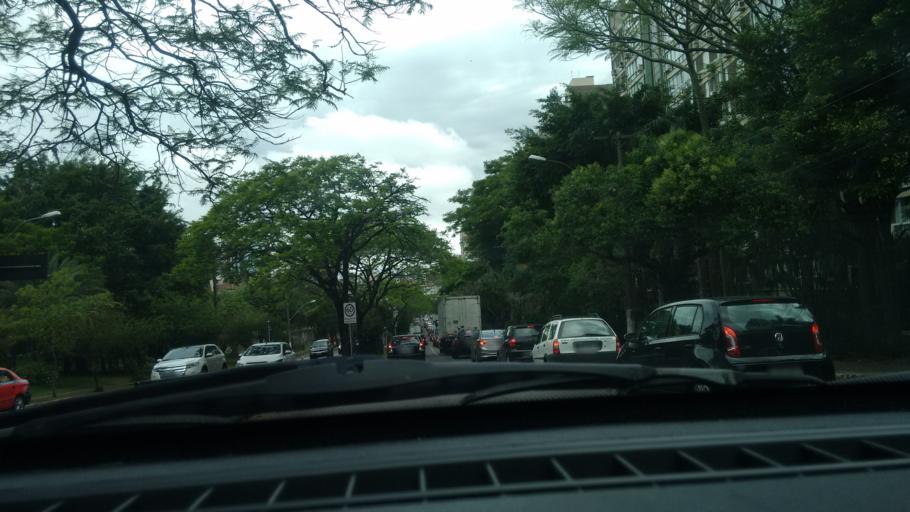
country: BR
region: Rio Grande do Sul
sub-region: Porto Alegre
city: Porto Alegre
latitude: -30.0322
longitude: -51.1840
